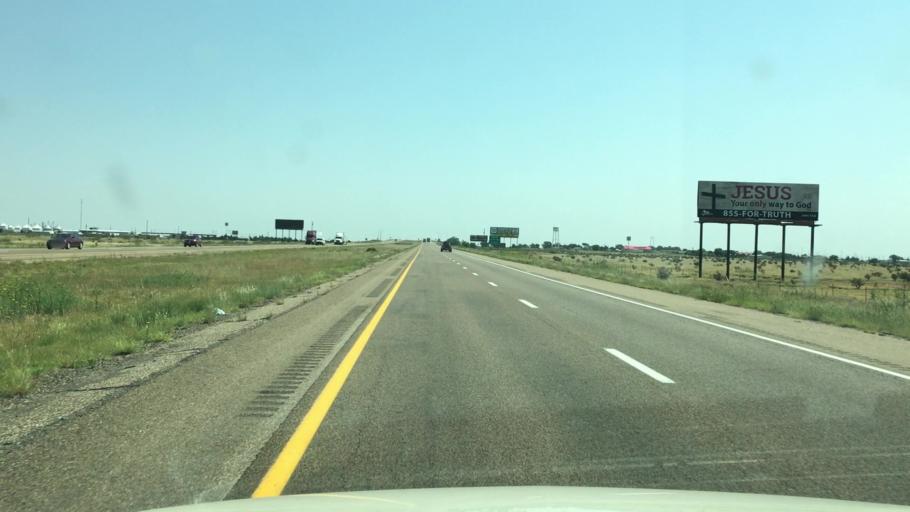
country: US
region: New Mexico
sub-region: Quay County
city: Logan
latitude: 35.1115
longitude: -103.3448
